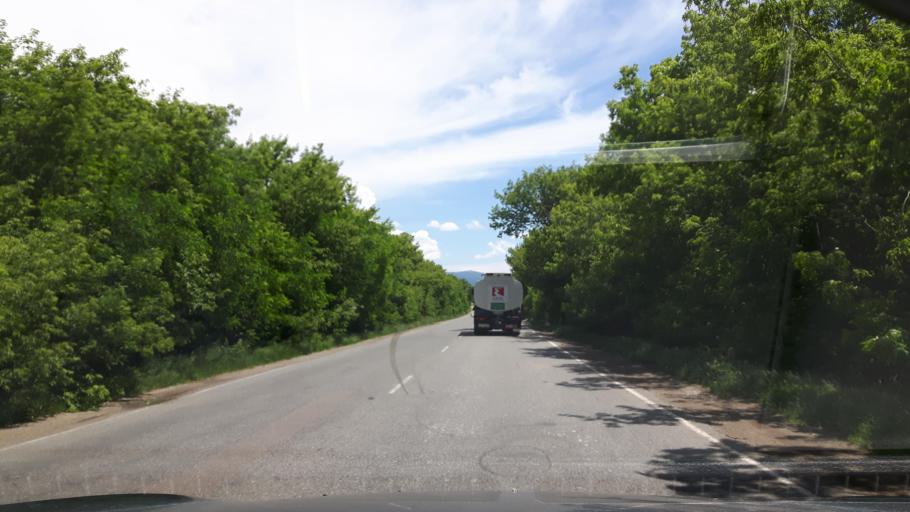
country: GE
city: Didi Lilo
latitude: 41.7082
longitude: 45.1394
